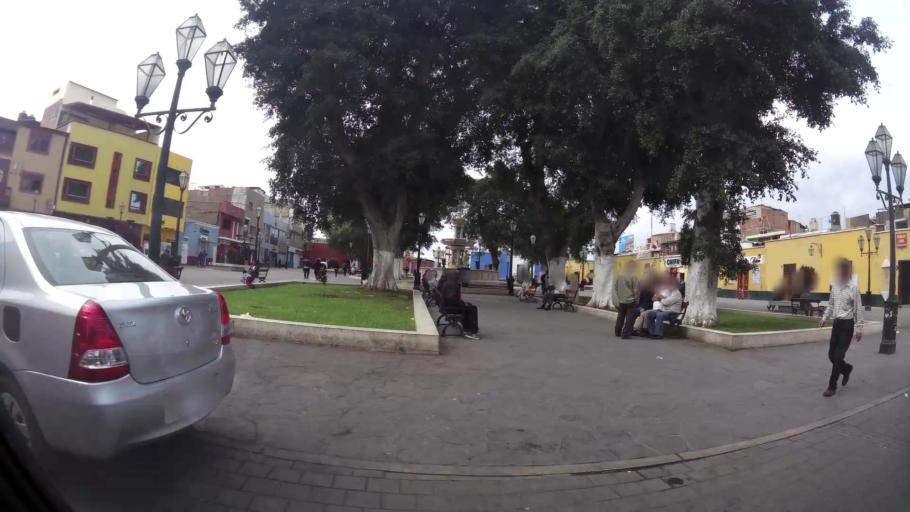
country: PE
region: La Libertad
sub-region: Provincia de Trujillo
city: Trujillo
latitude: -8.1075
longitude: -79.0242
